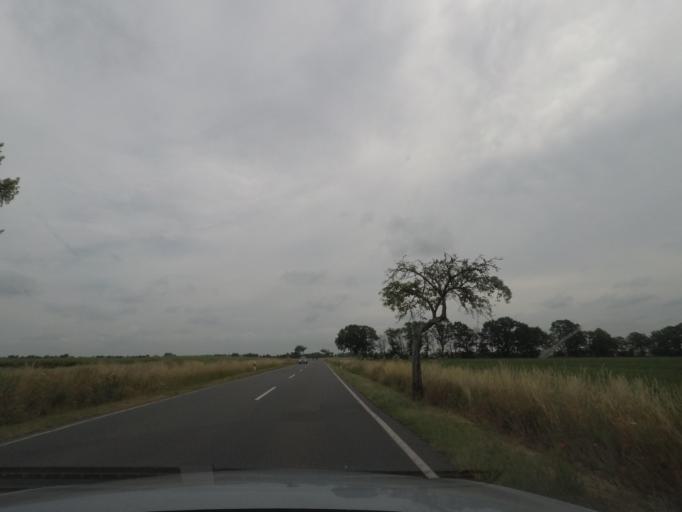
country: DE
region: Saxony-Anhalt
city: Hohendodeleben
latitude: 52.0779
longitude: 11.5045
